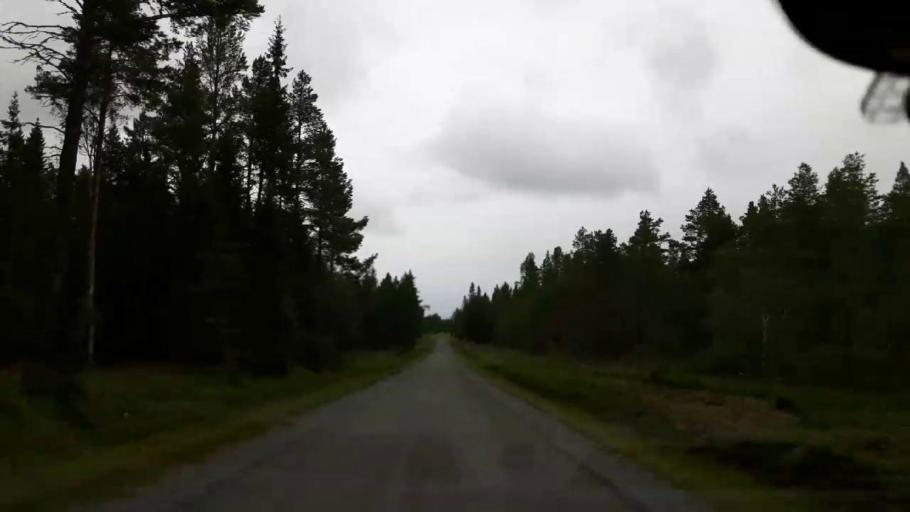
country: SE
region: Jaemtland
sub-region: OEstersunds Kommun
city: Ostersund
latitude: 63.0826
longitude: 14.5549
